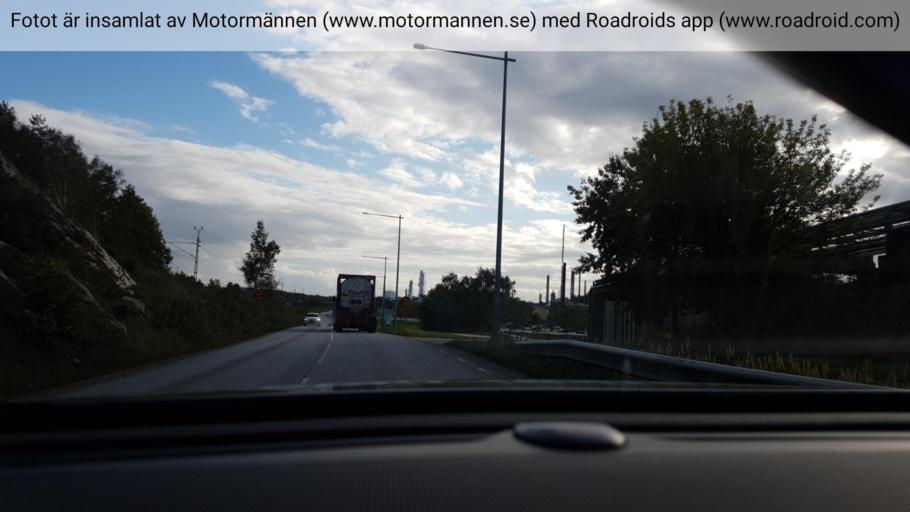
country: SE
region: Vaestra Goetaland
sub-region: Stenungsunds Kommun
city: Stenungsund
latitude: 58.0938
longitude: 11.8339
